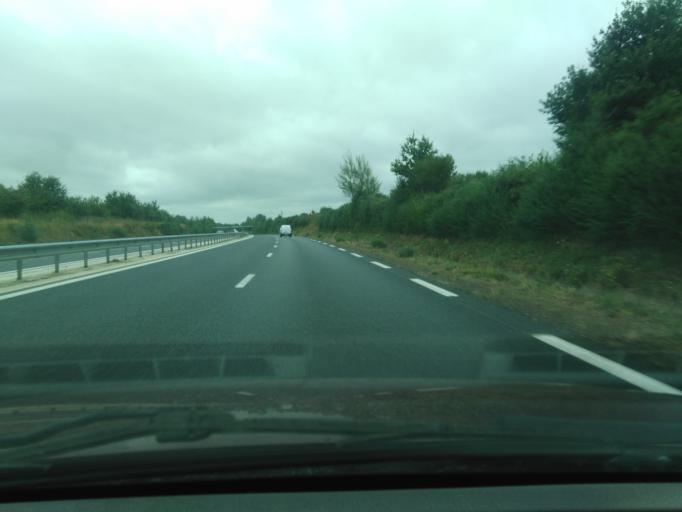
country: FR
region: Pays de la Loire
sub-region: Departement de la Vendee
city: La Roche-sur-Yon
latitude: 46.6797
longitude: -1.3812
